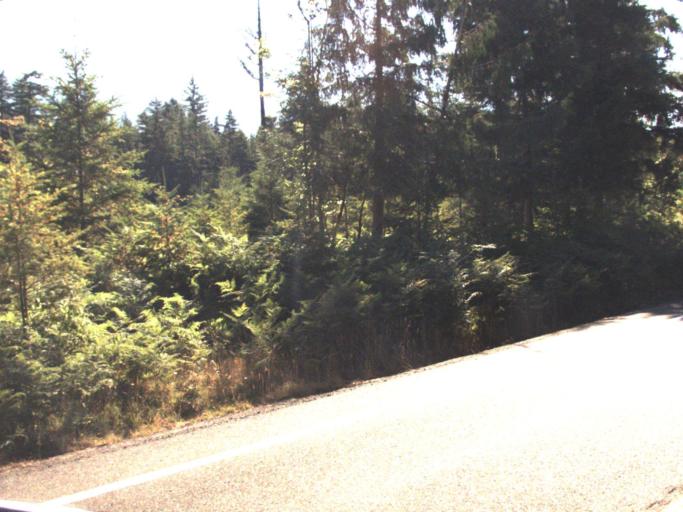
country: US
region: Washington
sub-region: King County
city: Riverbend
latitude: 47.1457
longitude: -121.6385
